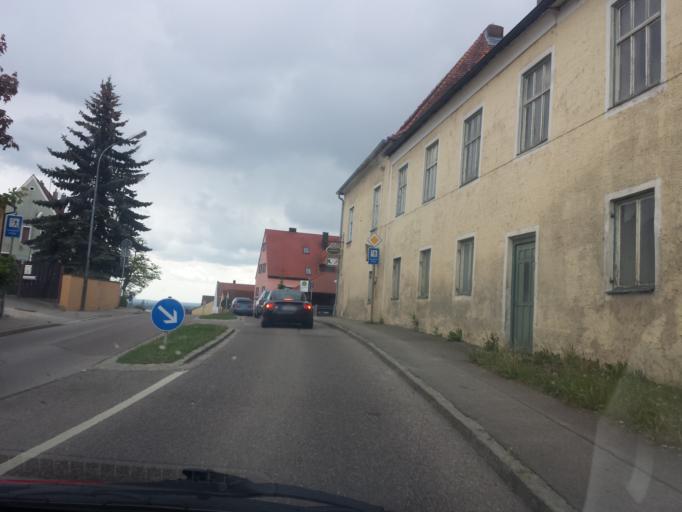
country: DE
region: Bavaria
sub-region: Upper Bavaria
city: Hepberg
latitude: 48.8234
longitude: 11.4610
